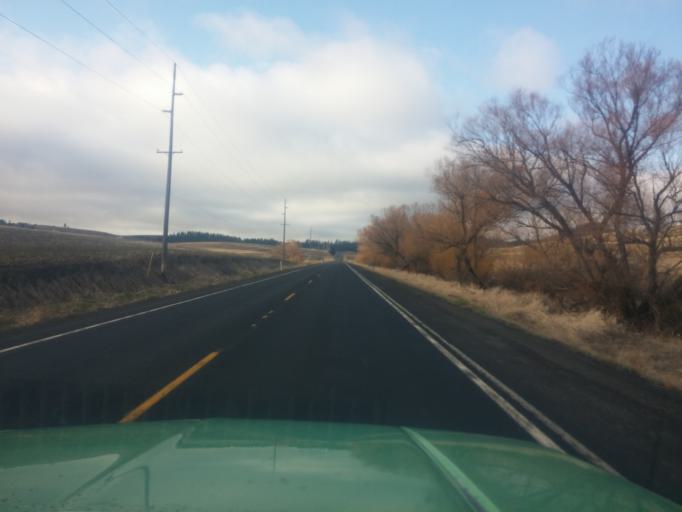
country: US
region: Idaho
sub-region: Latah County
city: Moscow
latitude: 46.8954
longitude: -116.9911
